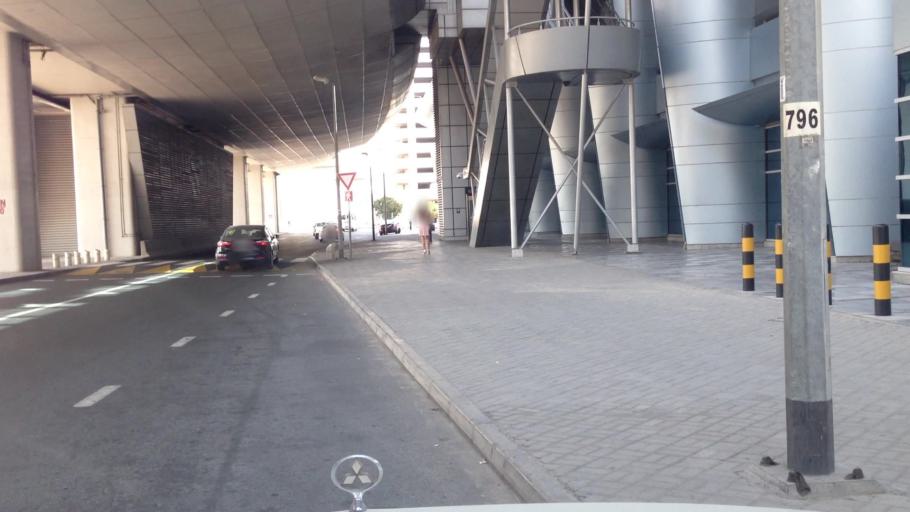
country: AE
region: Ash Shariqah
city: Sharjah
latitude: 25.2410
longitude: 55.3663
